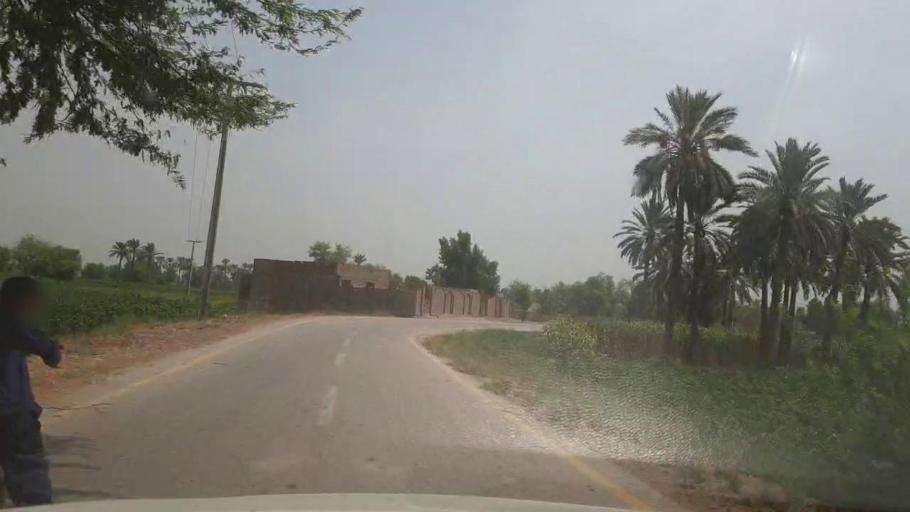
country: PK
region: Sindh
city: Kot Diji
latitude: 27.3698
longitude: 68.6459
